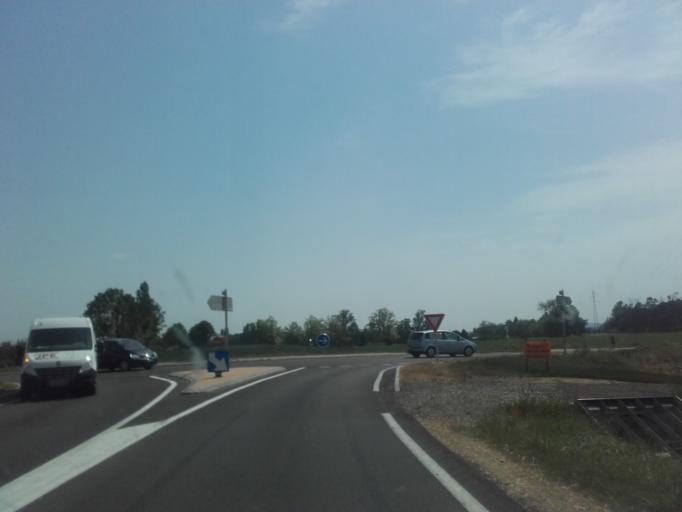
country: FR
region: Bourgogne
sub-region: Departement de la Cote-d'Or
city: Bligny-les-Beaune
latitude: 46.9636
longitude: 4.8174
